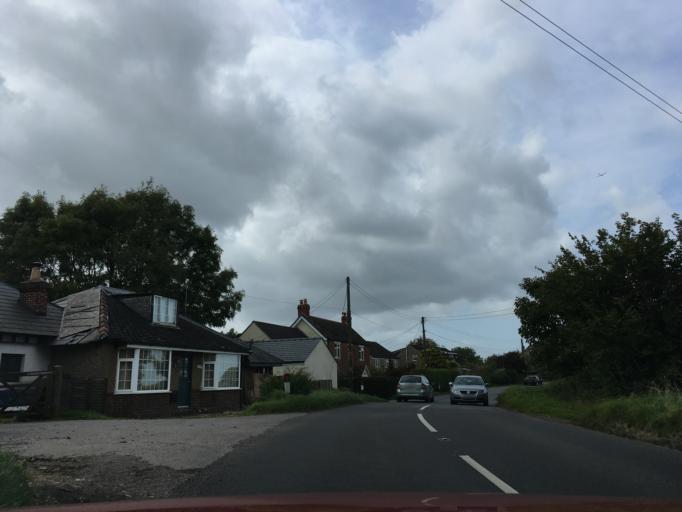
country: GB
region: England
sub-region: Gloucestershire
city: Stonehouse
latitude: 51.6996
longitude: -2.2914
